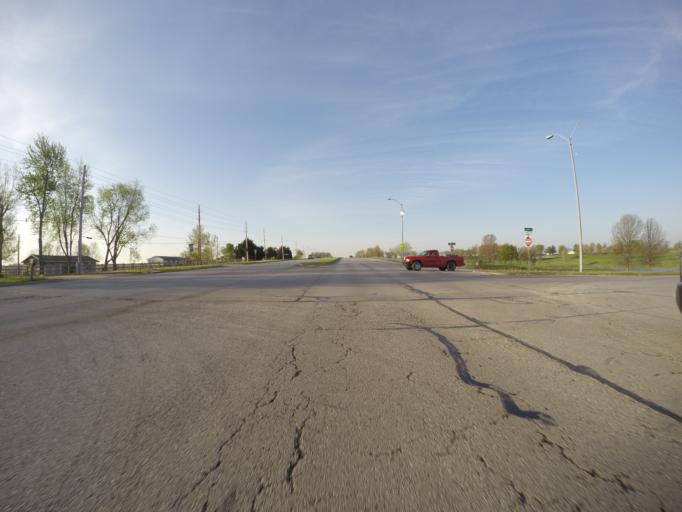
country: US
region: Missouri
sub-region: Jackson County
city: Lees Summit
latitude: 38.9240
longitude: -94.4502
